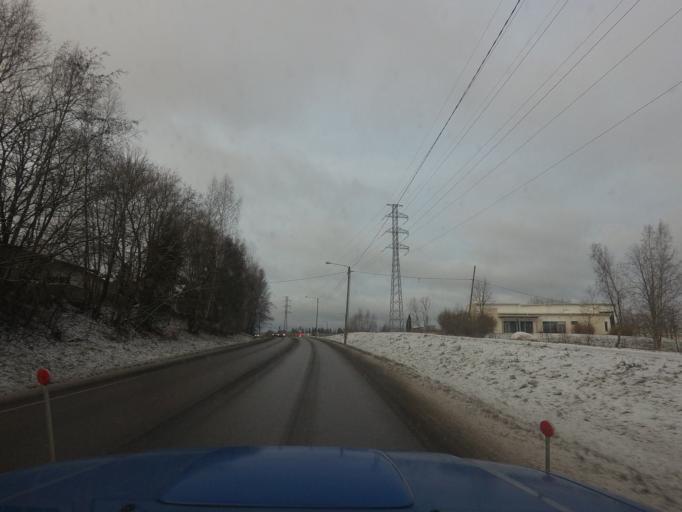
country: FI
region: Uusimaa
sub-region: Helsinki
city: Espoo
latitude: 60.1830
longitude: 24.6052
